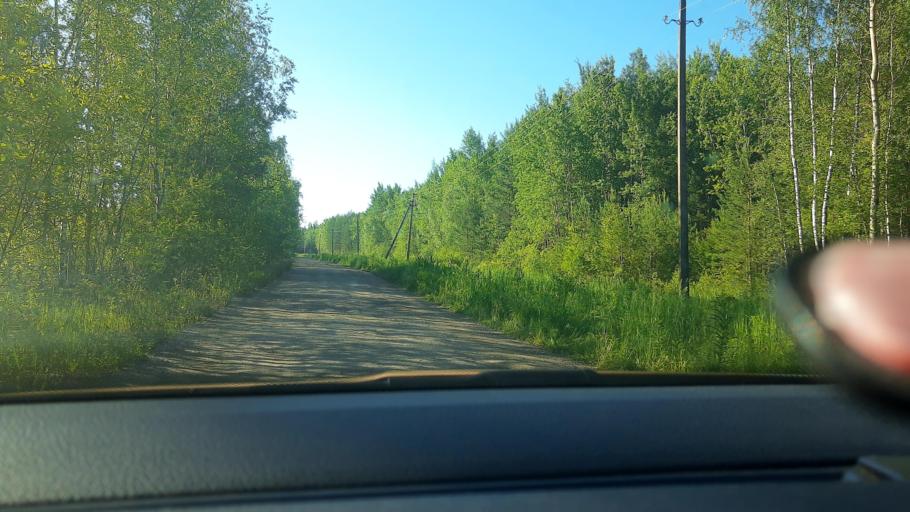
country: RU
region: Moskovskaya
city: Elektrogorsk
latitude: 55.8965
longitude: 38.7153
